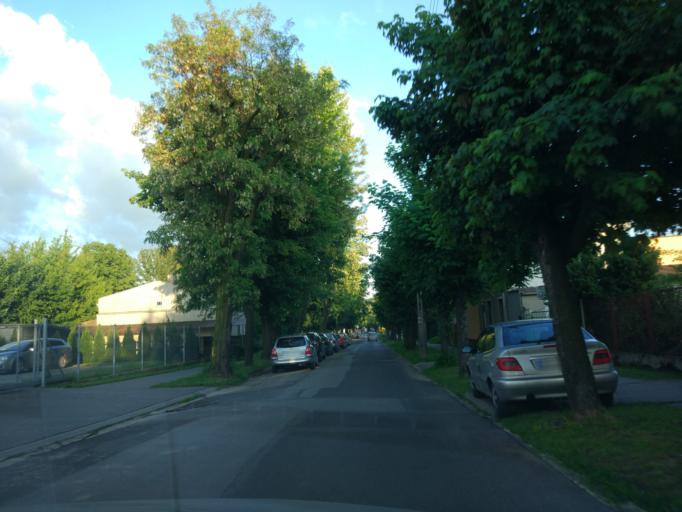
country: PL
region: Lodz Voivodeship
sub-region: Powiat kutnowski
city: Kutno
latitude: 52.2321
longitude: 19.3497
